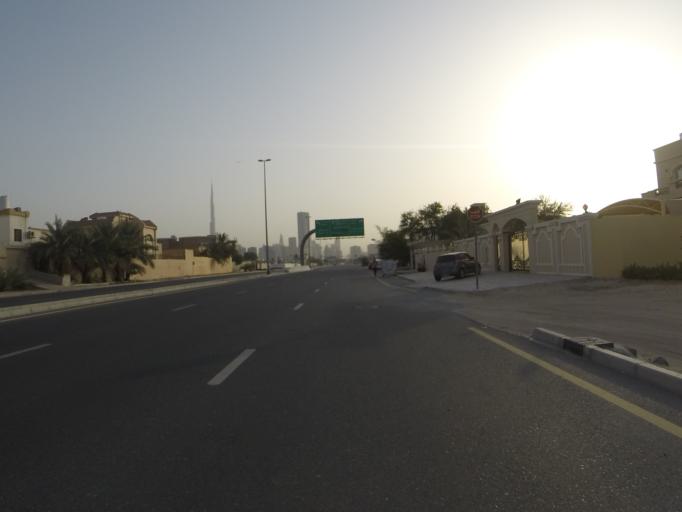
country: AE
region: Dubai
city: Dubai
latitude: 25.1639
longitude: 55.2582
